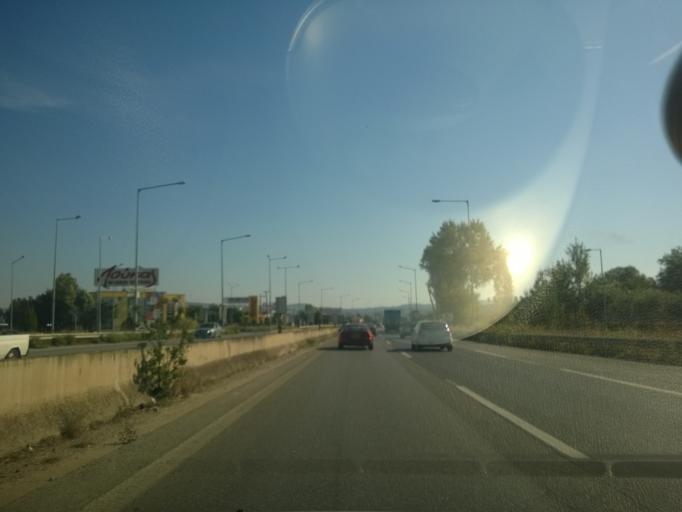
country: GR
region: Central Macedonia
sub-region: Nomos Thessalonikis
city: Thermi
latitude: 40.5314
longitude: 23.0127
